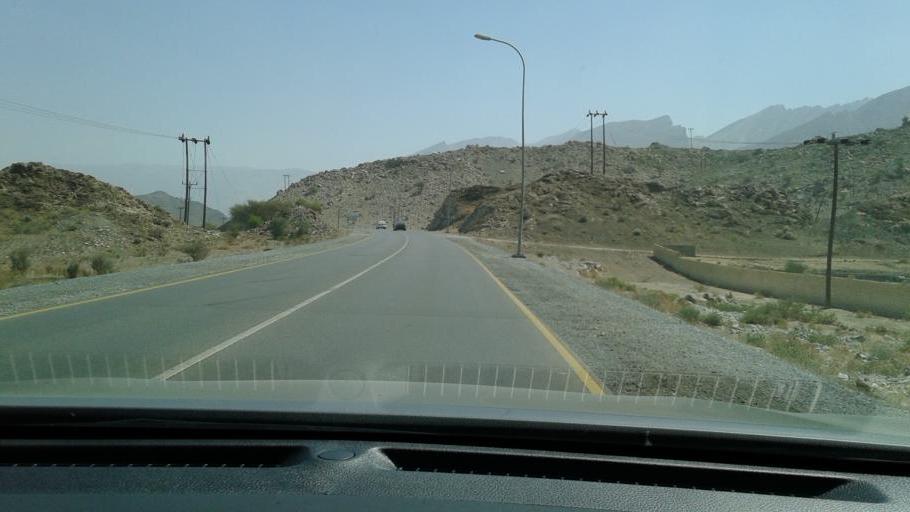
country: OM
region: Al Batinah
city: Rustaq
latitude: 23.3716
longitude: 57.4550
